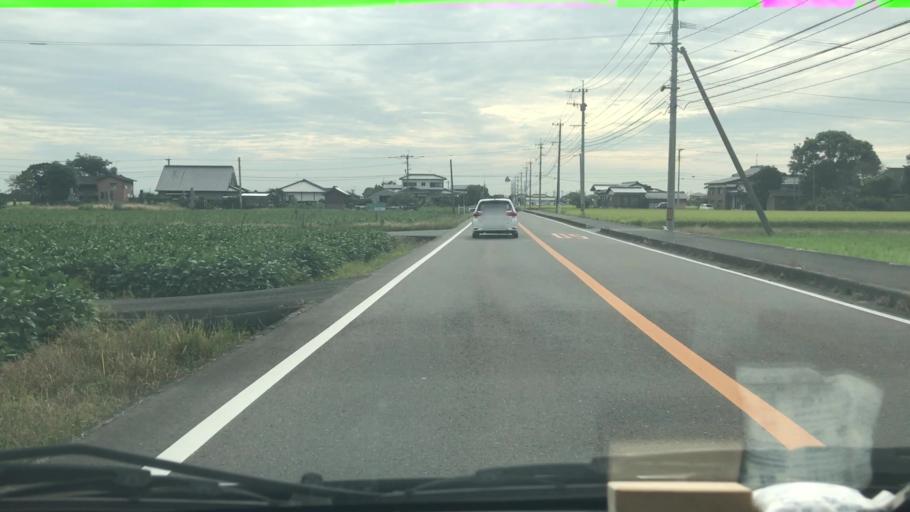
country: JP
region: Saga Prefecture
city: Takeocho-takeo
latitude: 33.1974
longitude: 130.1073
